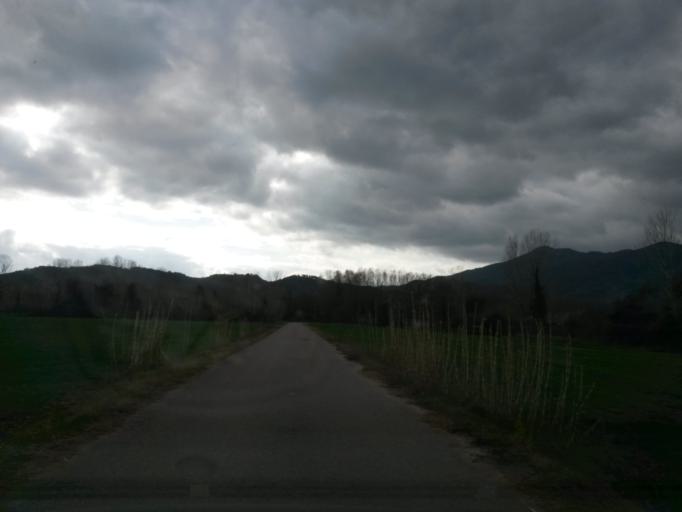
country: ES
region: Catalonia
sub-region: Provincia de Girona
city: Angles
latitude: 41.9657
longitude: 2.6484
